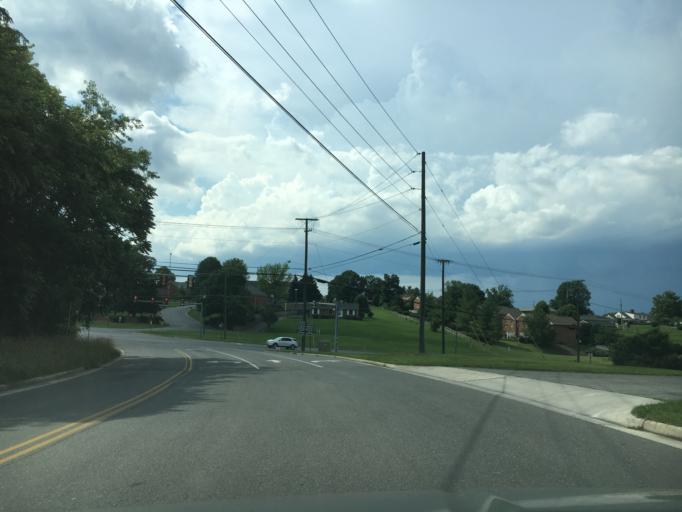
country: US
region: Virginia
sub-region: Roanoke County
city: Cave Spring
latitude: 37.2173
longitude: -80.0168
